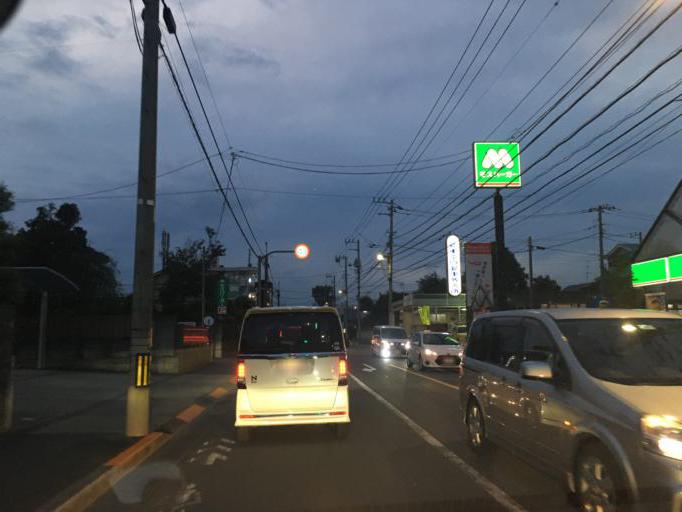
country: JP
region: Tokyo
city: Higashimurayama-shi
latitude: 35.7308
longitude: 139.4580
